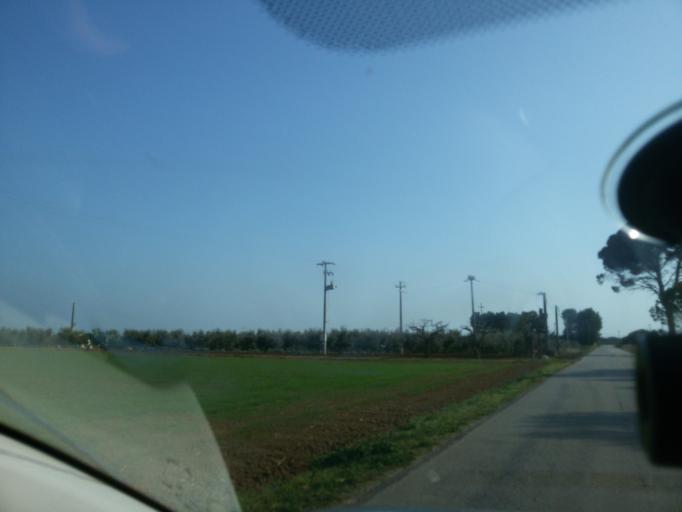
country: IT
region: Apulia
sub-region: Provincia di Brindisi
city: Mesagne
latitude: 40.5928
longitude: 17.8156
